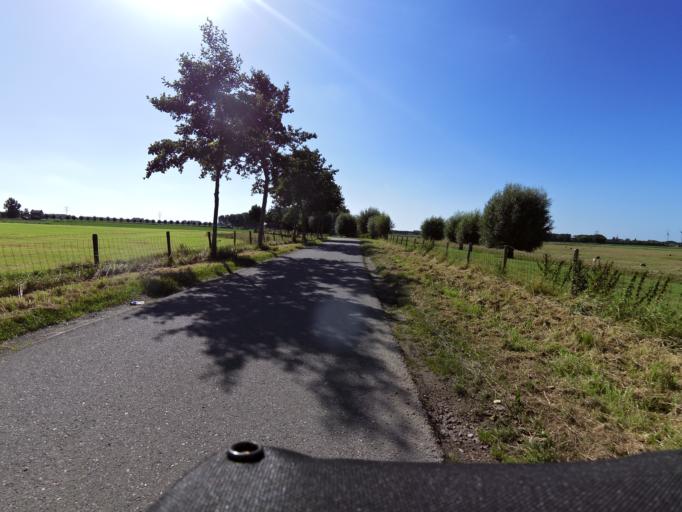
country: NL
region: South Holland
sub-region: Gemeente Spijkenisse
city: Spijkenisse
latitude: 51.8497
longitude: 4.2770
